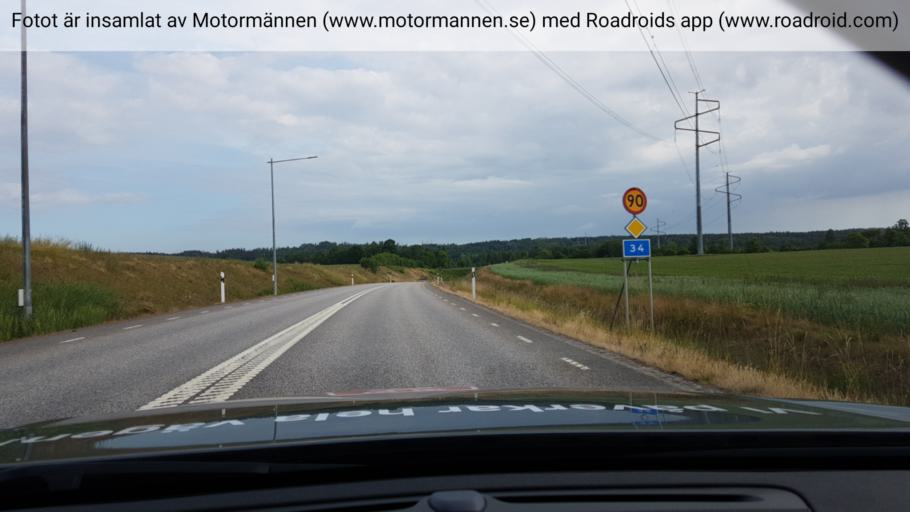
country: SE
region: OEstergoetland
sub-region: Motala Kommun
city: Borensberg
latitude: 58.5461
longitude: 15.3204
